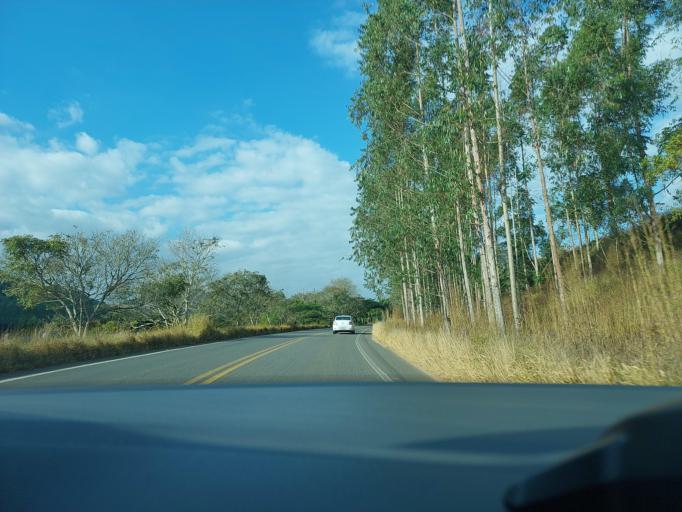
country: BR
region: Minas Gerais
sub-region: Vicosa
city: Vicosa
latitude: -20.8275
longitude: -42.7821
